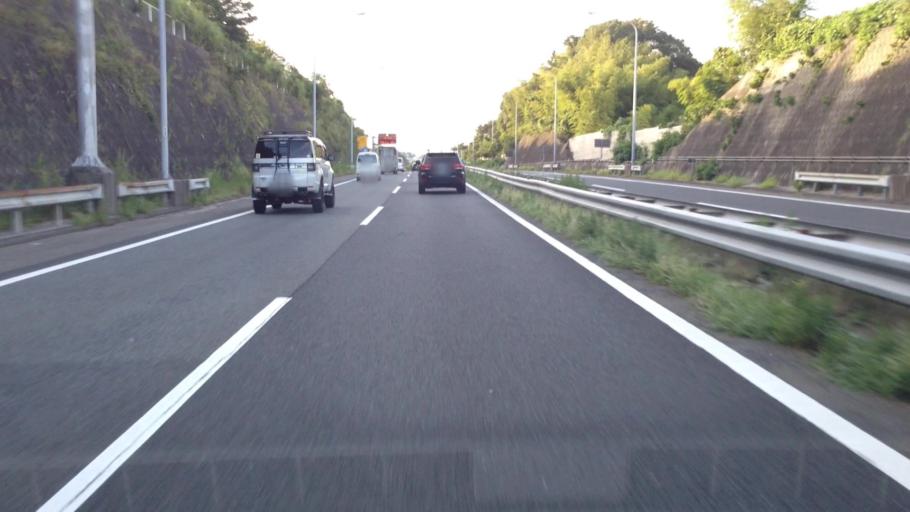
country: JP
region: Kanagawa
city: Kamakura
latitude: 35.3774
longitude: 139.5880
